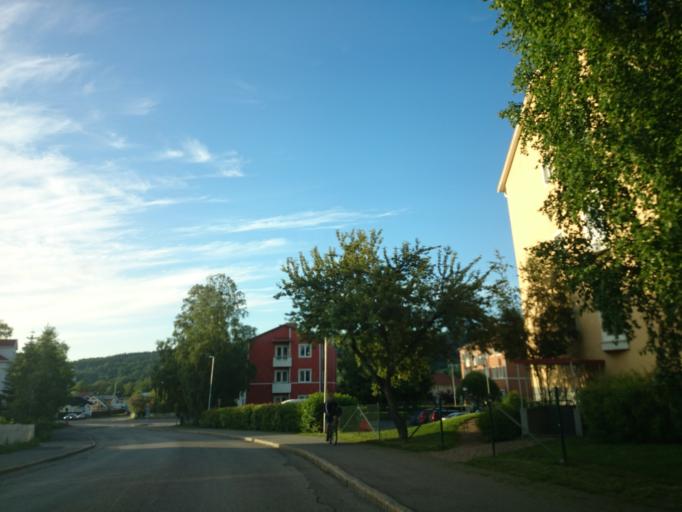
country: SE
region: Vaesternorrland
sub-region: Sundsvalls Kommun
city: Sundsvall
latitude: 62.3875
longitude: 17.2830
